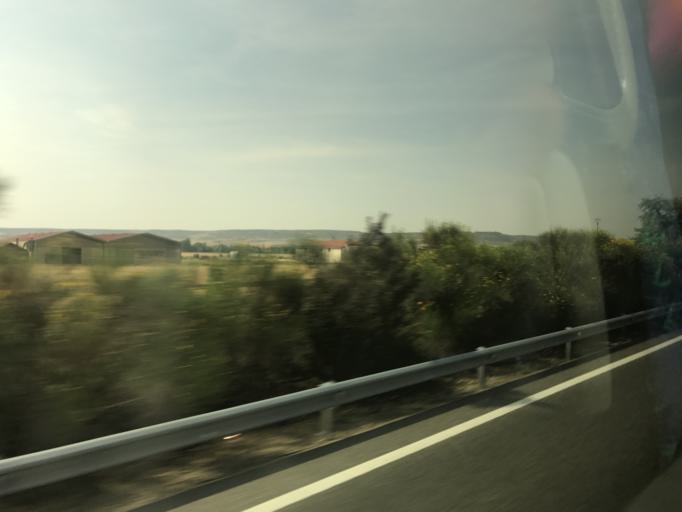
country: ES
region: Castille and Leon
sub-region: Provincia de Palencia
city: Villodrigo
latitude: 42.1468
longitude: -4.1011
